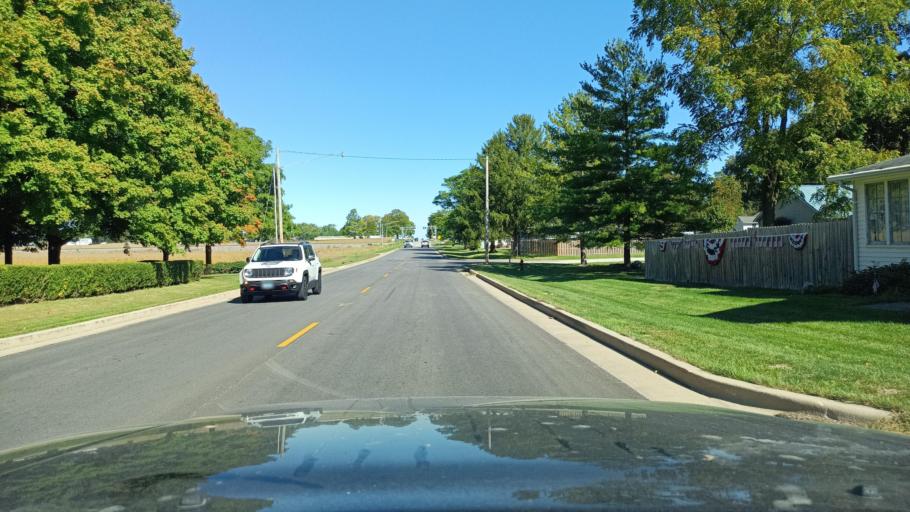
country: US
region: Illinois
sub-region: Champaign County
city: Philo
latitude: 40.0041
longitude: -88.1613
